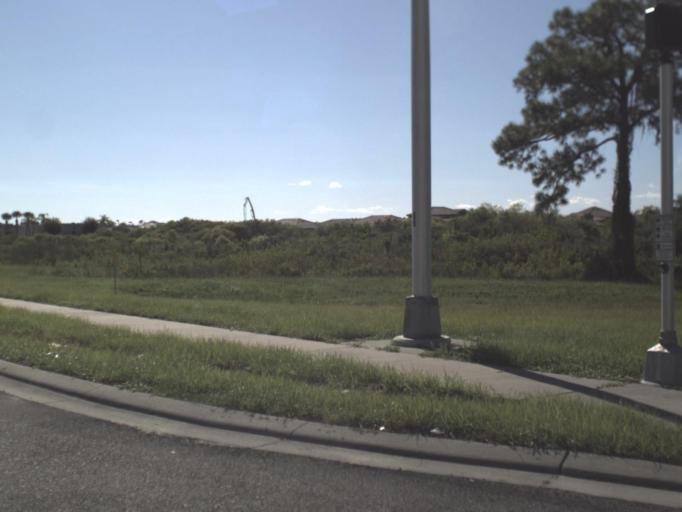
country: US
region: Florida
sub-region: Lee County
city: Fort Myers
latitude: 26.6344
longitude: -81.8015
